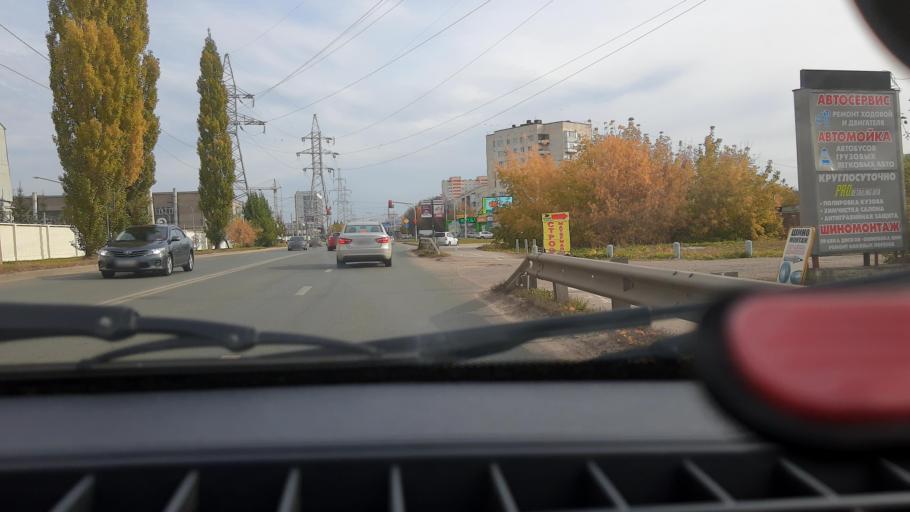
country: RU
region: Bashkortostan
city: Ufa
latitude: 54.7884
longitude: 56.1190
